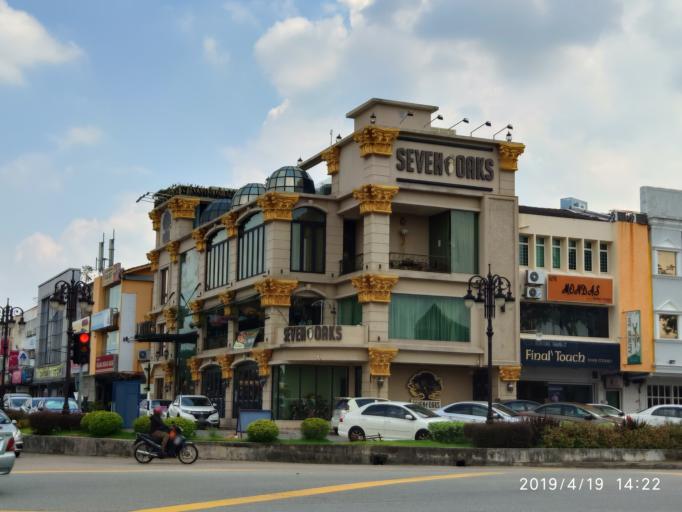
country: MY
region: Johor
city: Johor Bahru
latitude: 1.4846
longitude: 103.7716
